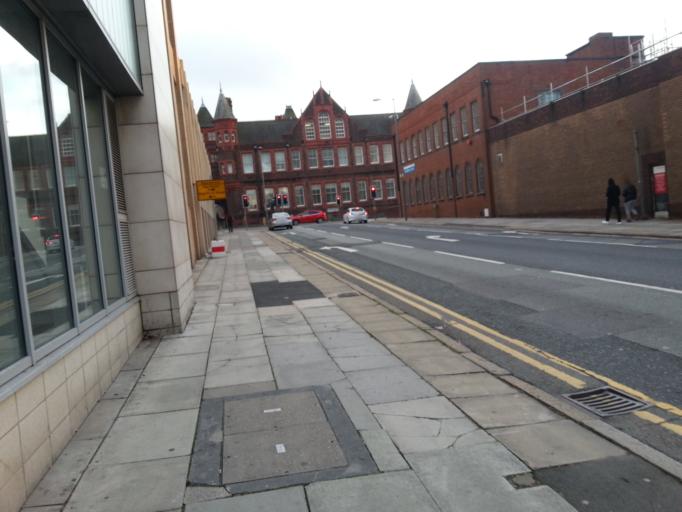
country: GB
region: England
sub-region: Liverpool
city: Liverpool
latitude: 53.4093
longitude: -2.9679
